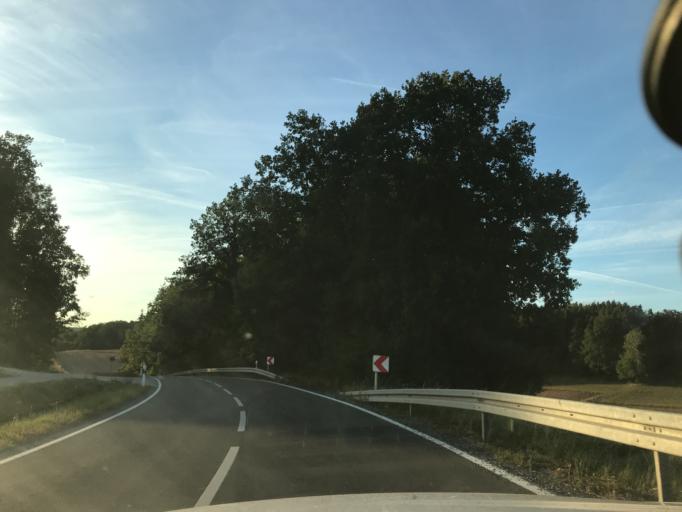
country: DE
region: Bavaria
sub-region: Upper Franconia
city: Pegnitz
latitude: 49.7192
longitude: 11.5720
